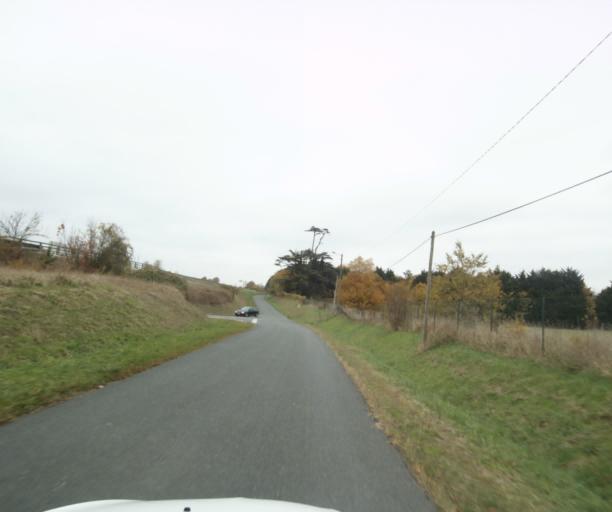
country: FR
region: Poitou-Charentes
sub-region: Departement de la Charente-Maritime
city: Les Gonds
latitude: 45.7307
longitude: -0.6174
